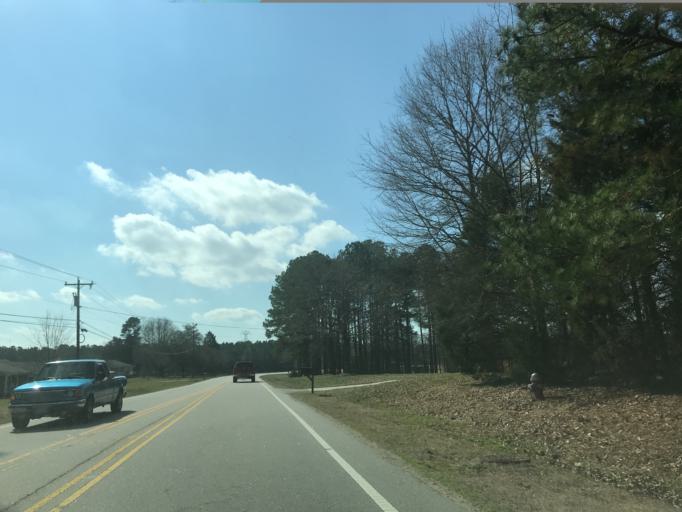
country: US
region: North Carolina
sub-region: Durham County
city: Gorman
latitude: 35.9646
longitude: -78.8068
